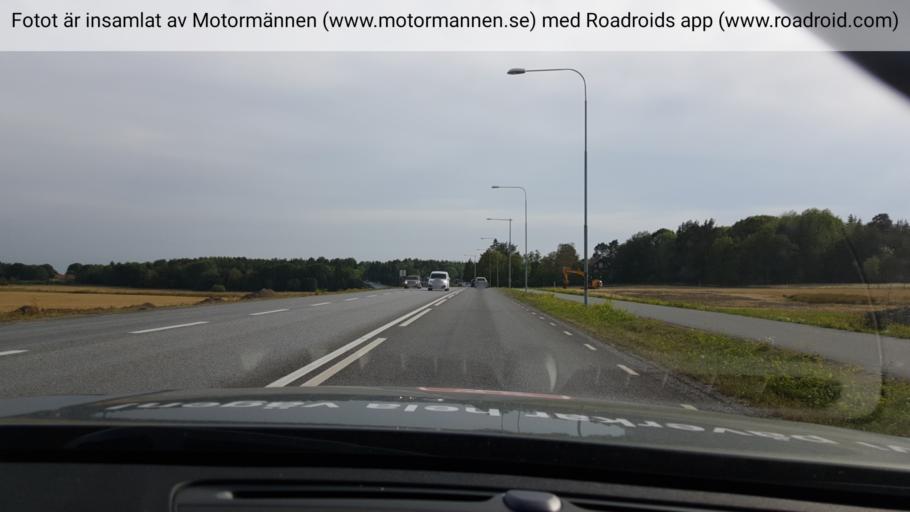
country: SE
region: Stockholm
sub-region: Ekero Kommun
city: Ekeroe
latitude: 59.3188
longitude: 17.8655
